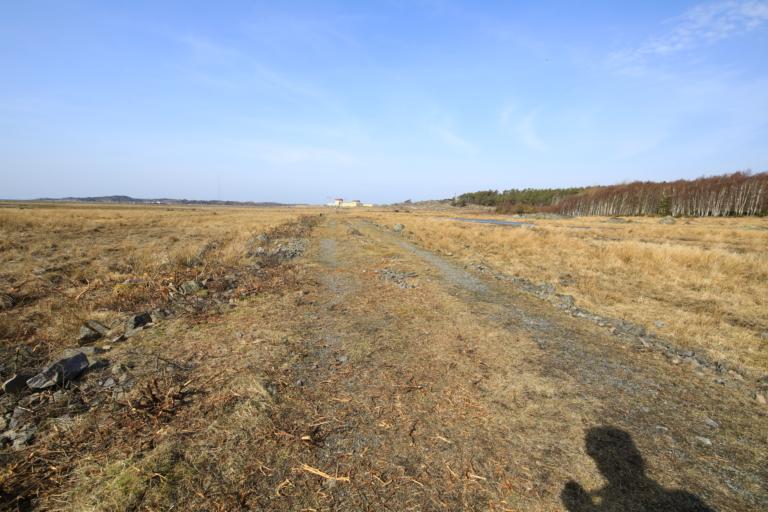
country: SE
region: Halland
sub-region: Kungsbacka Kommun
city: Frillesas
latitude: 57.2503
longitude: 12.1334
